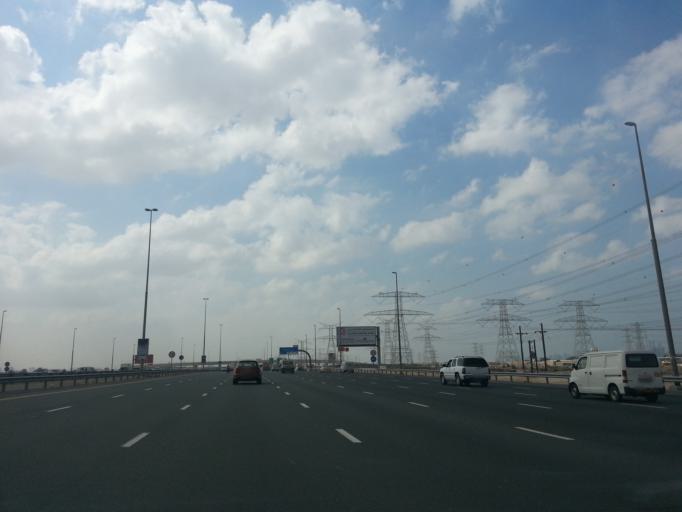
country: AE
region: Dubai
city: Dubai
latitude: 25.1090
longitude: 55.2389
